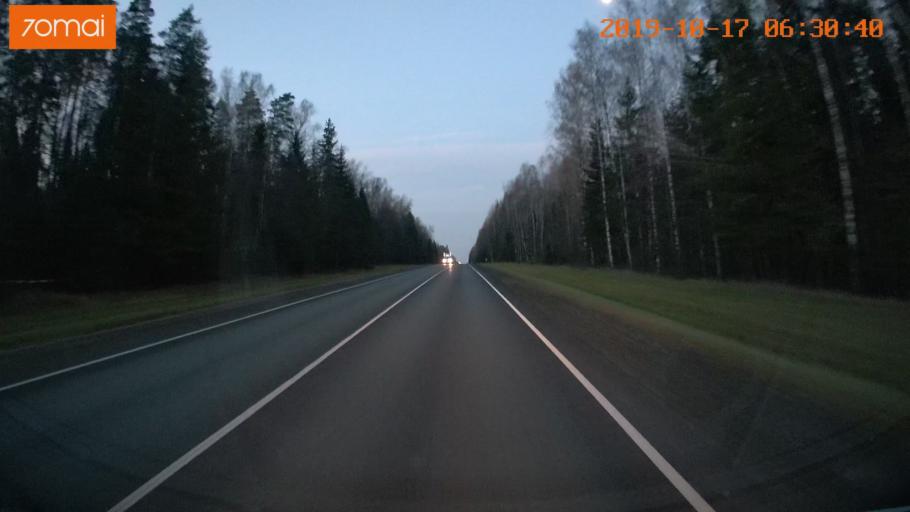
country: RU
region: Ivanovo
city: Lezhnevo
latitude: 56.7342
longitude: 40.7147
